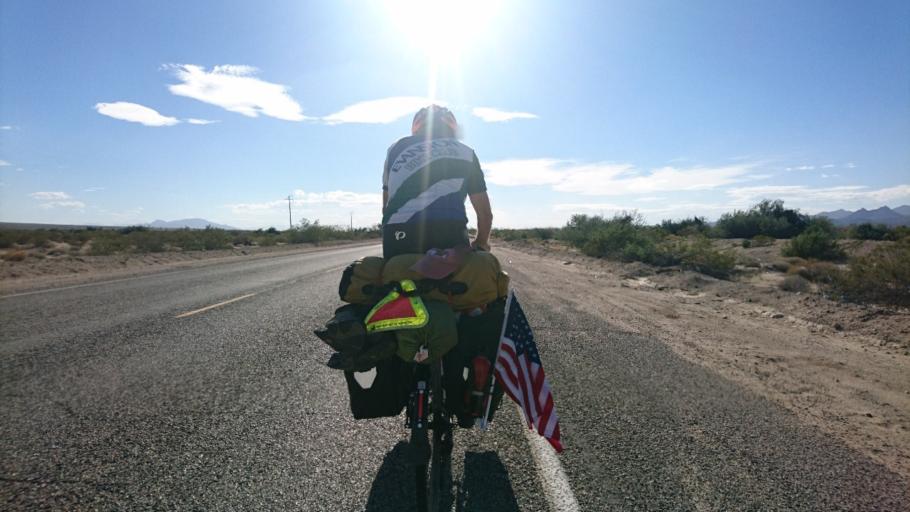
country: US
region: California
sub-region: San Bernardino County
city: Needles
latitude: 34.7194
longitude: -115.2713
